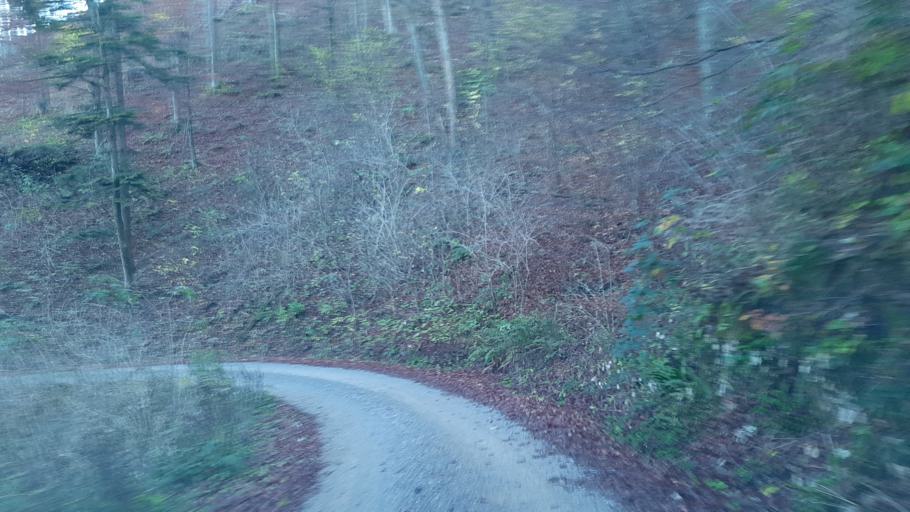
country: SI
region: Borovnica
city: Borovnica
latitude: 45.9264
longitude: 14.3419
